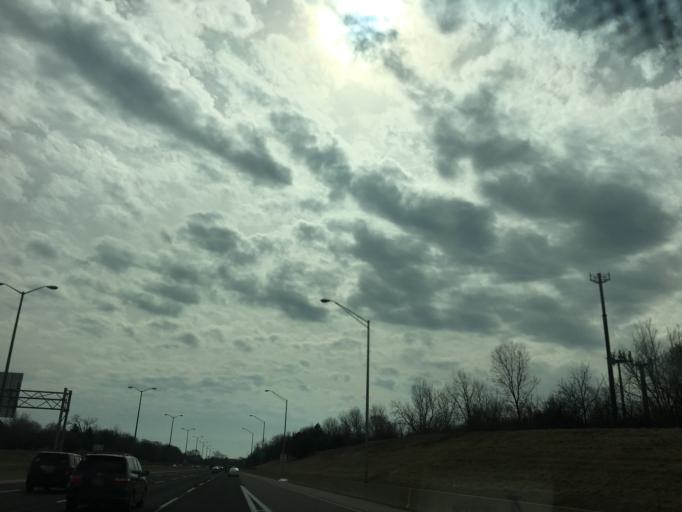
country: US
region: Illinois
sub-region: DuPage County
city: Woodridge
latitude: 41.7689
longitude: -88.0428
